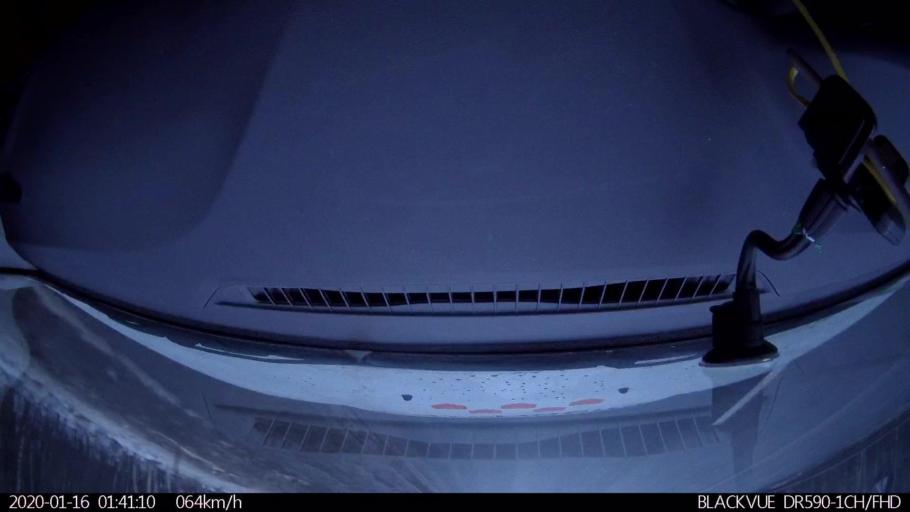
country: RU
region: Nizjnij Novgorod
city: Gorbatovka
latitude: 56.3214
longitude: 43.7715
